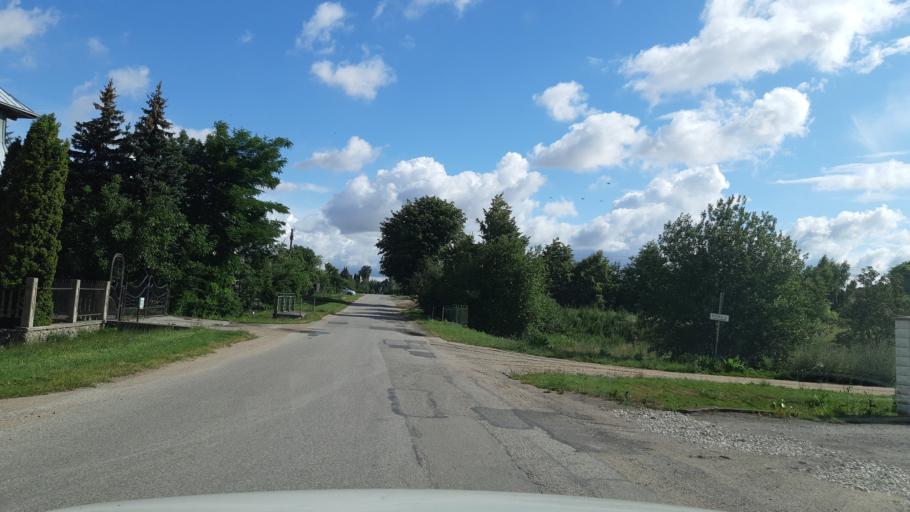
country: LT
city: Vilkaviskis
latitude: 54.6371
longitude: 23.0538
